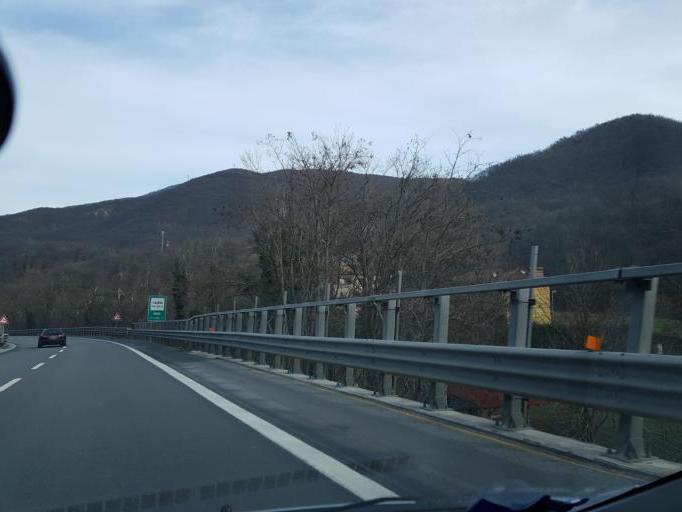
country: IT
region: Liguria
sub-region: Provincia di Genova
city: Isola del Cantone
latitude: 44.6453
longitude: 8.9594
